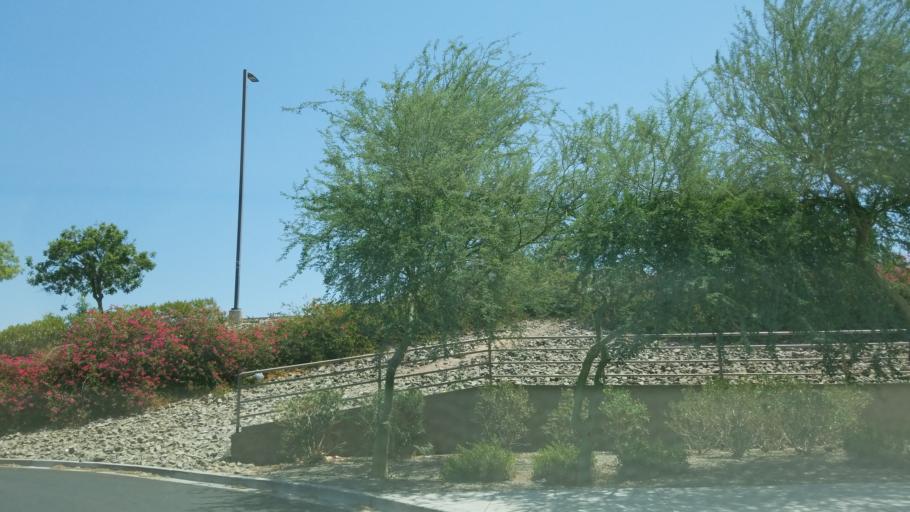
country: US
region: Arizona
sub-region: Maricopa County
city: Peoria
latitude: 33.6430
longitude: -112.2241
